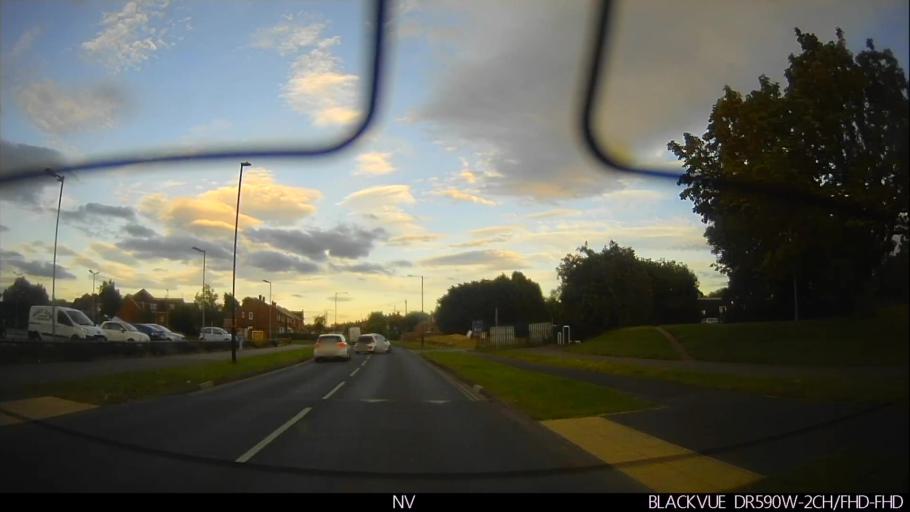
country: GB
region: England
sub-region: City of York
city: Bishopthorpe
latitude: 53.9438
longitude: -1.1210
